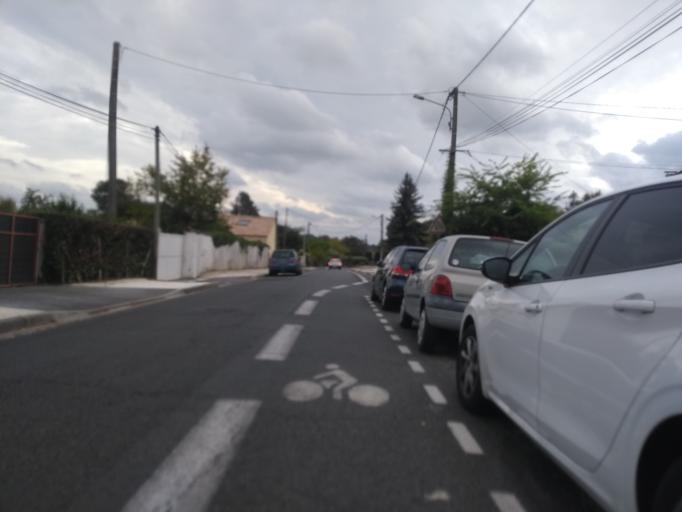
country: FR
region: Aquitaine
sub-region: Departement de la Gironde
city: Gradignan
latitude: 44.7805
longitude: -0.5945
